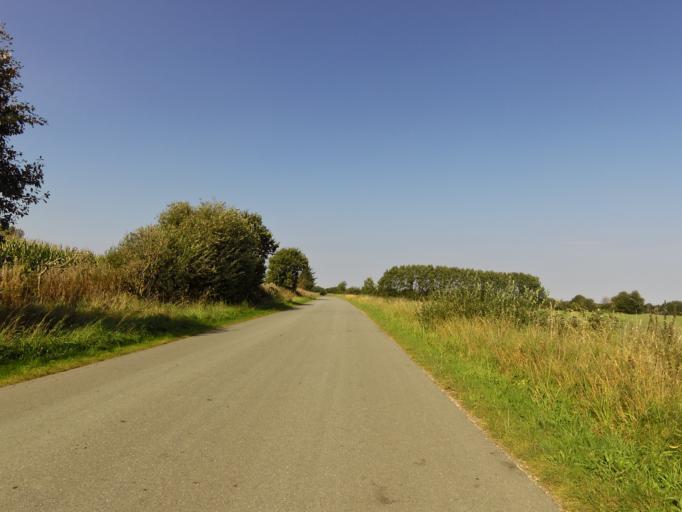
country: DK
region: South Denmark
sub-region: Vejen Kommune
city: Rodding
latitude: 55.3723
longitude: 9.1366
